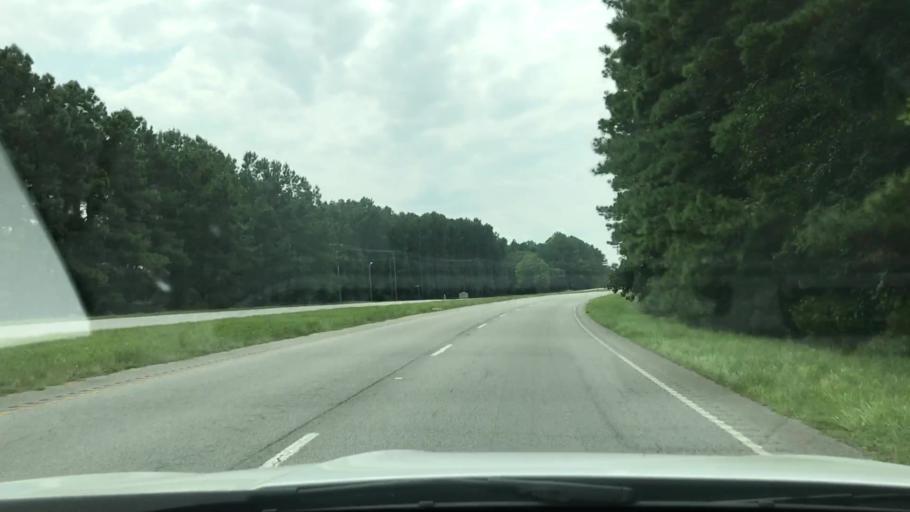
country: US
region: South Carolina
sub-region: Charleston County
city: Awendaw
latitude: 32.9474
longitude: -79.6999
